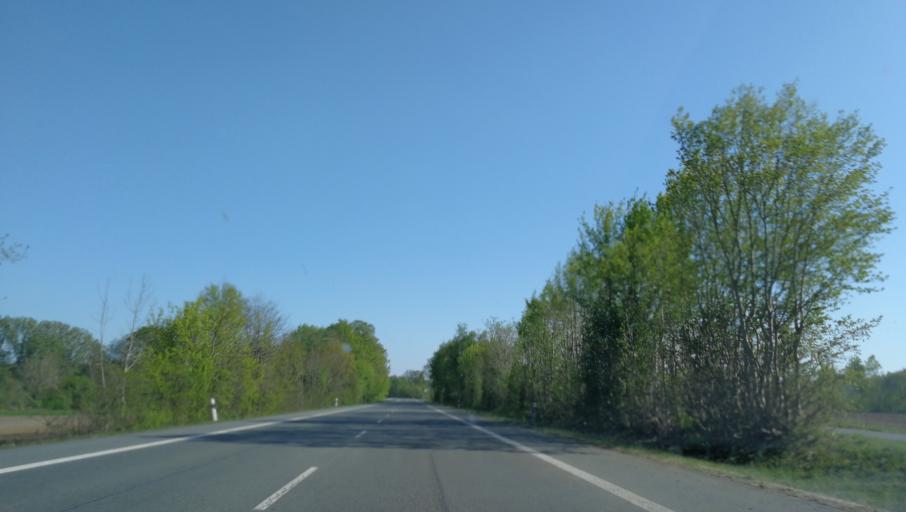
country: DE
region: North Rhine-Westphalia
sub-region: Regierungsbezirk Munster
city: Rheine
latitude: 52.2531
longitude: 7.4605
